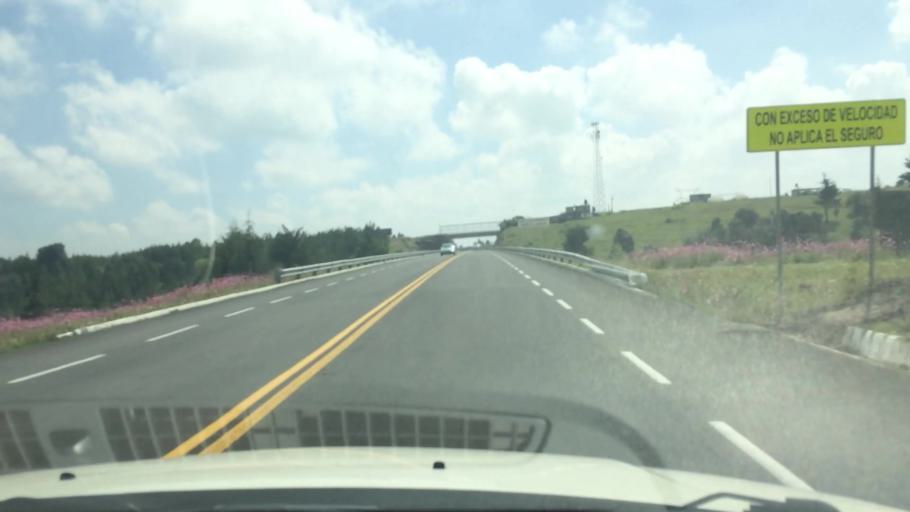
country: MX
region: Mexico
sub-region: Villa Victoria
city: Colonia Doctor Gustavo Baz
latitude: 19.3765
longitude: -99.8992
